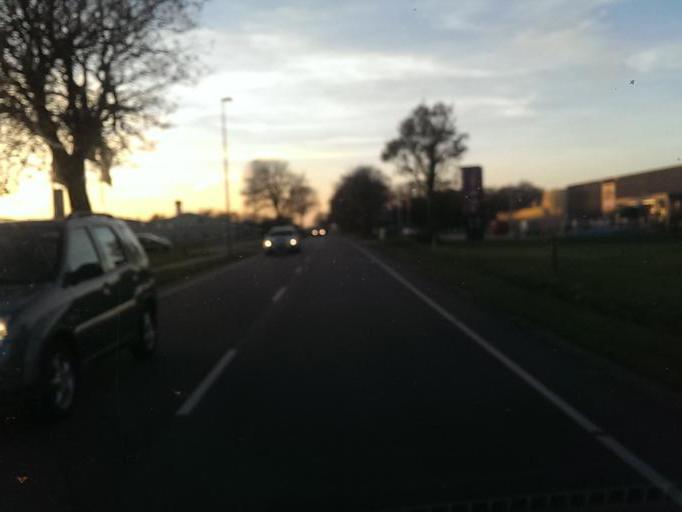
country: DK
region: South Denmark
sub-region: Esbjerg Kommune
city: Bramming
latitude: 55.4680
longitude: 8.6815
